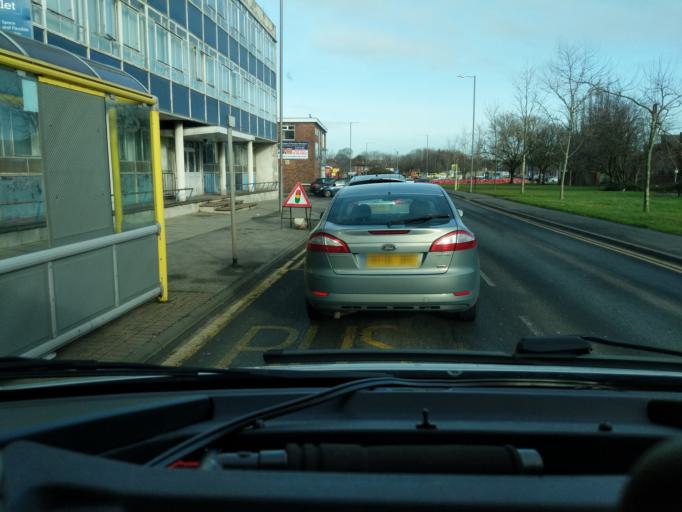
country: GB
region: England
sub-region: St. Helens
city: St Helens
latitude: 53.4573
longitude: -2.7371
